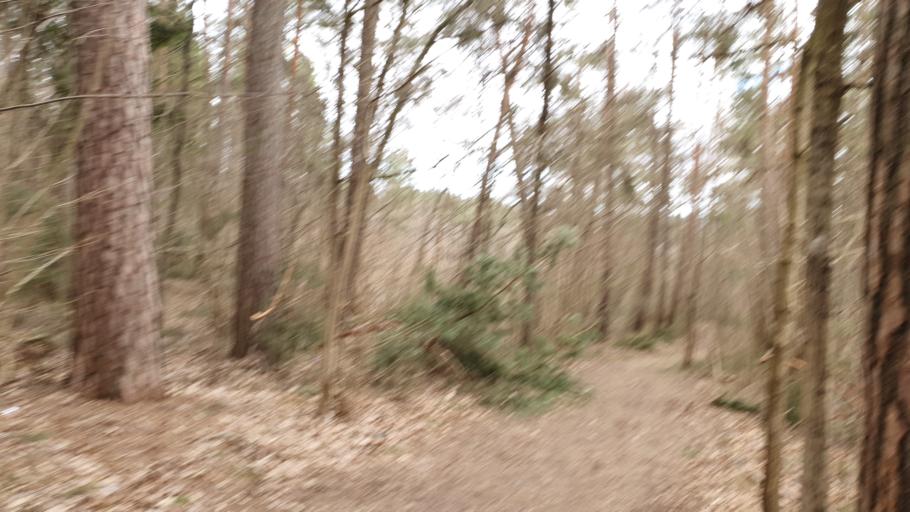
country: LT
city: Grigiskes
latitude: 54.7374
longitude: 25.0253
